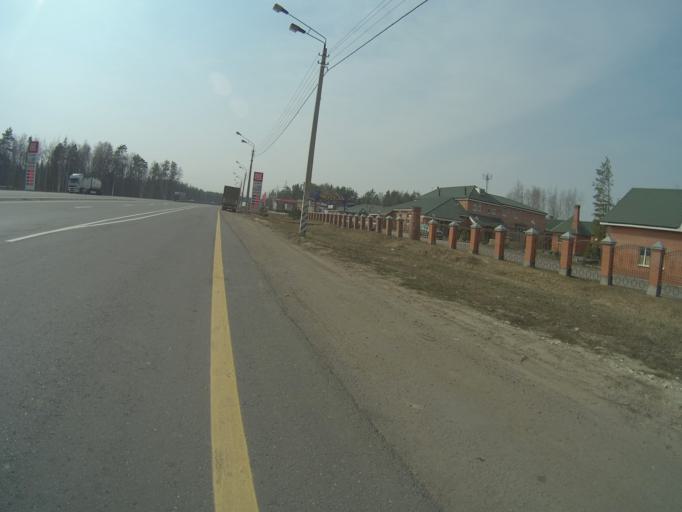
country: RU
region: Vladimir
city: Kommunar
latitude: 56.0631
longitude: 40.4561
